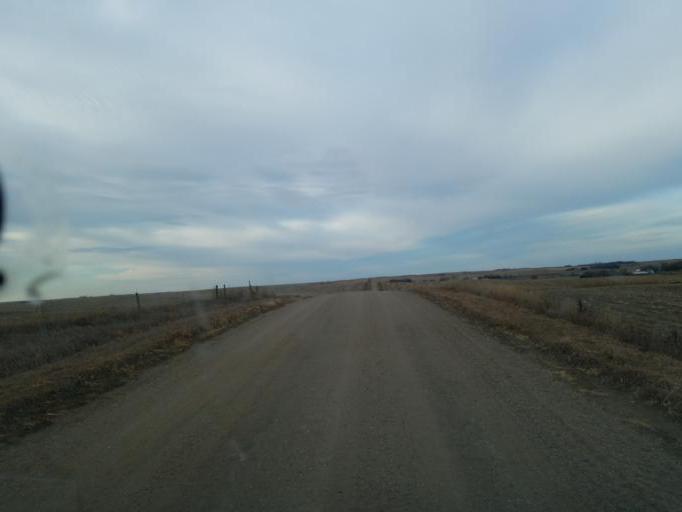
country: US
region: Nebraska
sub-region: Knox County
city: Bloomfield
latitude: 42.5688
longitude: -97.6510
